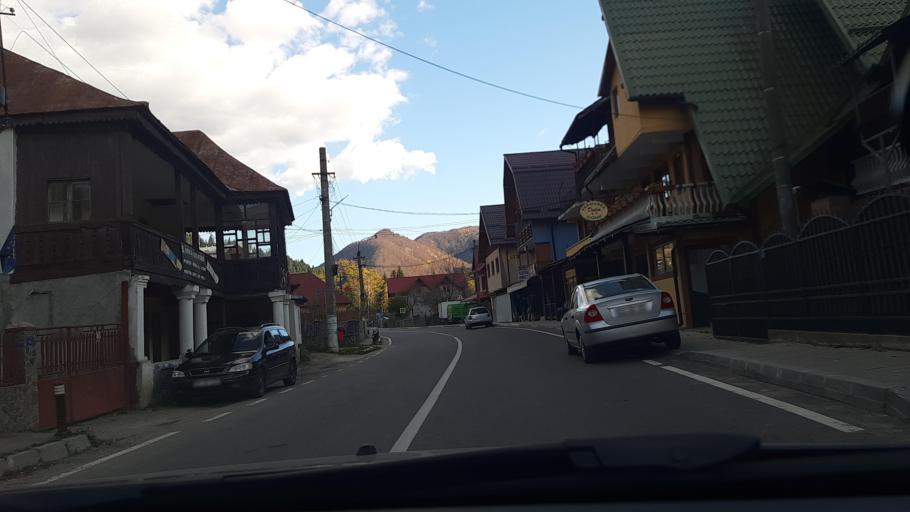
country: RO
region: Valcea
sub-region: Comuna Voineasa
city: Voineasa
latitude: 45.4191
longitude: 23.9574
